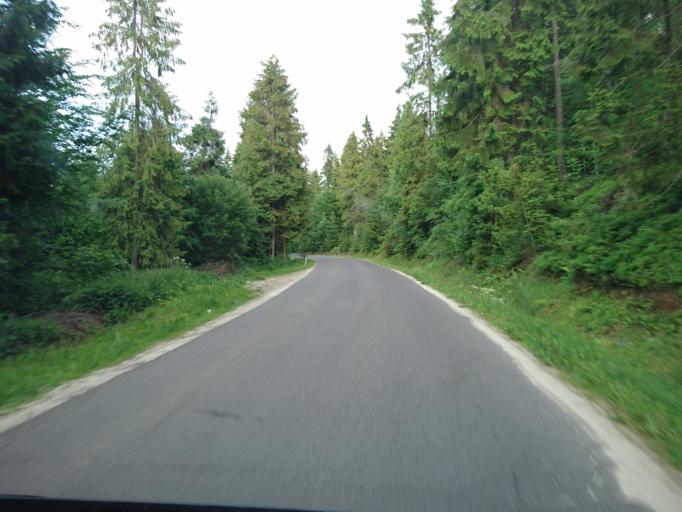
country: PL
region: Lesser Poland Voivodeship
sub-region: Powiat nowotarski
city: Lopuszna
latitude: 49.5032
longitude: 20.1853
